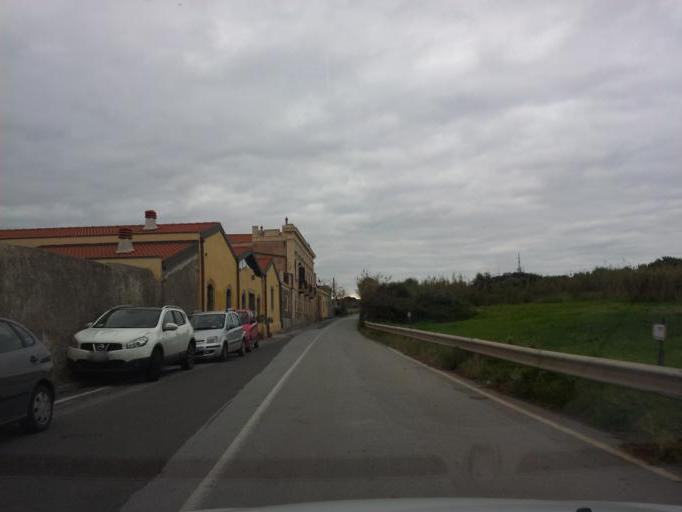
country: IT
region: Sicily
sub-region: Messina
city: Milazzo
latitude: 38.2639
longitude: 15.2382
